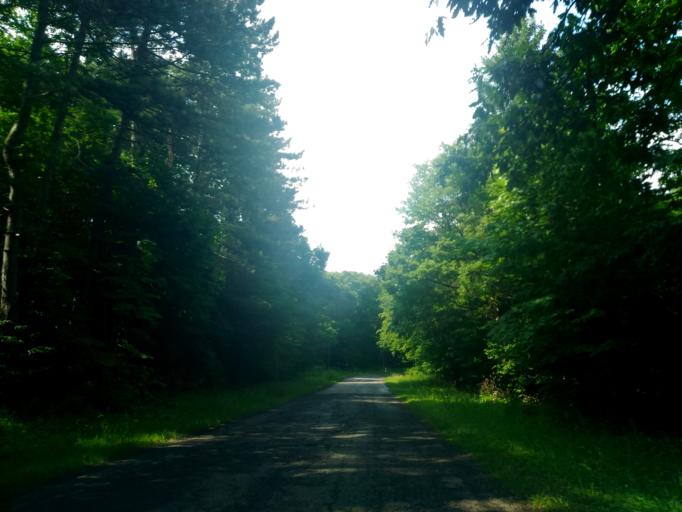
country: HU
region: Baranya
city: Pecs
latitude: 46.1256
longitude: 18.2254
